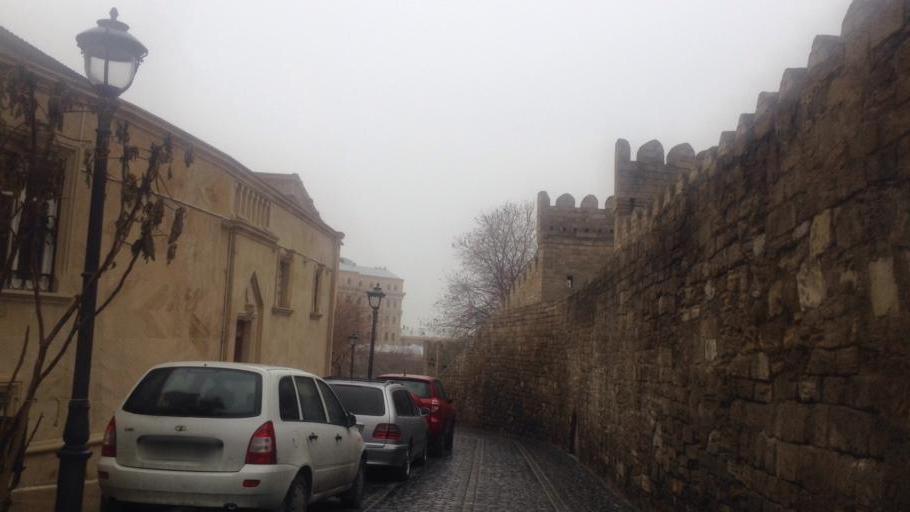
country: AZ
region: Baki
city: Badamdar
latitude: 40.3649
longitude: 49.8324
